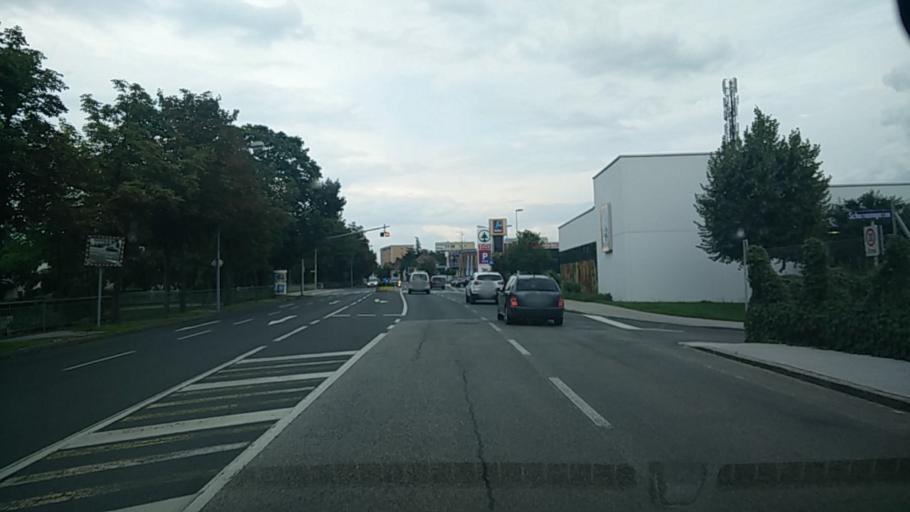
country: AT
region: Carinthia
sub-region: Klagenfurt am Woerthersee
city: Klagenfurt am Woerthersee
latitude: 46.6197
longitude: 14.2761
